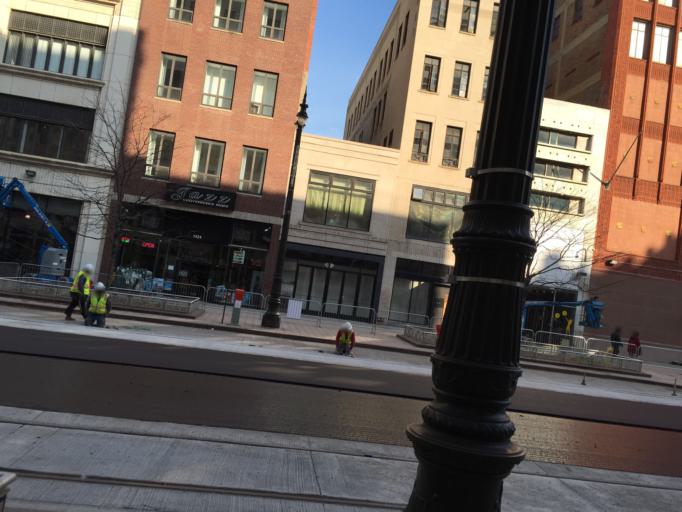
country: US
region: Michigan
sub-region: Wayne County
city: Detroit
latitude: 42.3345
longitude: -83.0492
